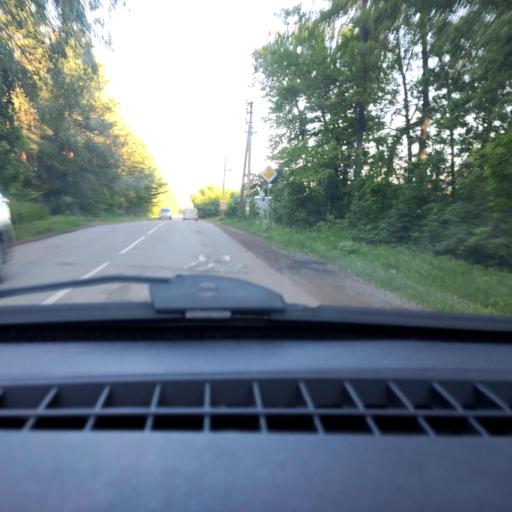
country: RU
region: Bashkortostan
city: Avdon
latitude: 54.6471
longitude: 55.7031
